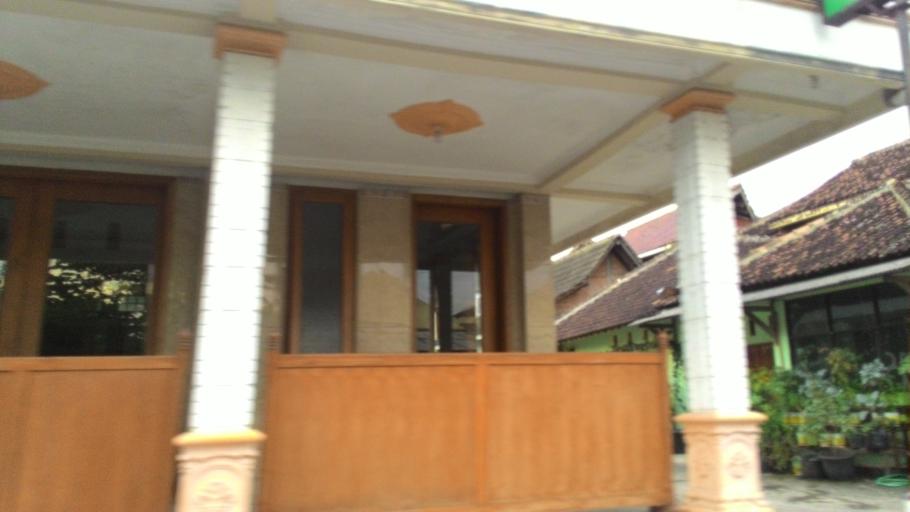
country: ID
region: Daerah Istimewa Yogyakarta
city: Depok
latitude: -7.8282
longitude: 110.4424
